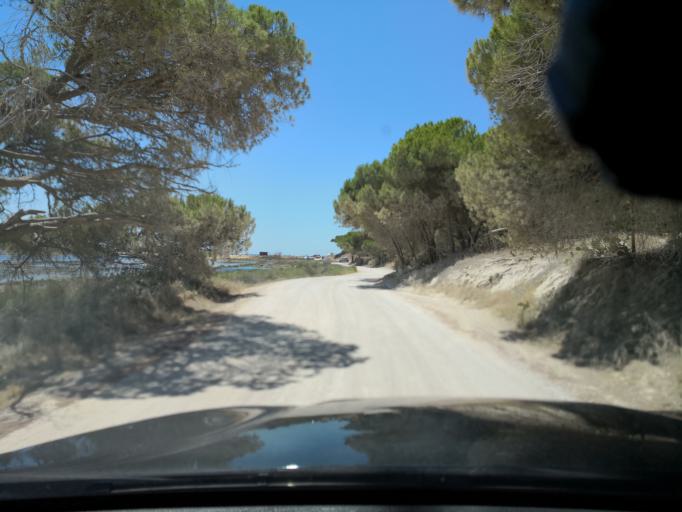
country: PT
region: Faro
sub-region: Loule
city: Quarteira
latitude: 37.0618
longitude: -8.0841
